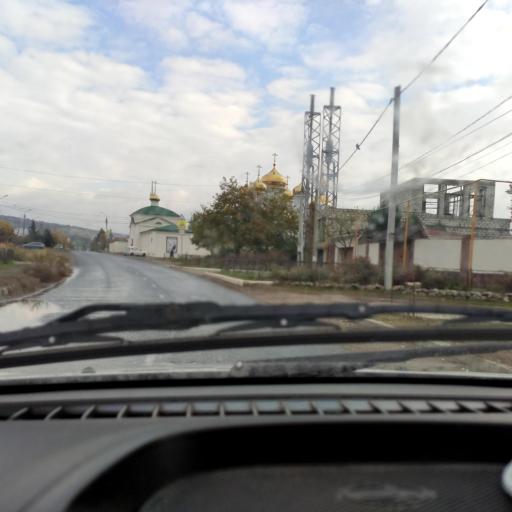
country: RU
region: Samara
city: Zhigulevsk
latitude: 53.4641
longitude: 49.6286
